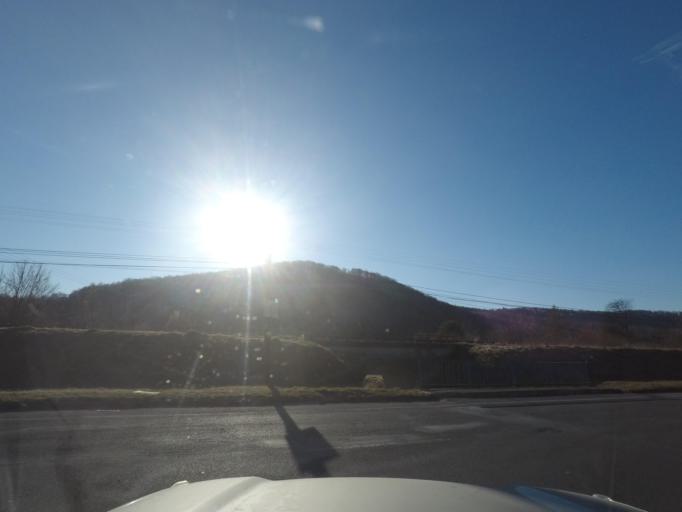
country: SK
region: Presovsky
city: Medzilaborce
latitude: 49.2532
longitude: 21.9117
